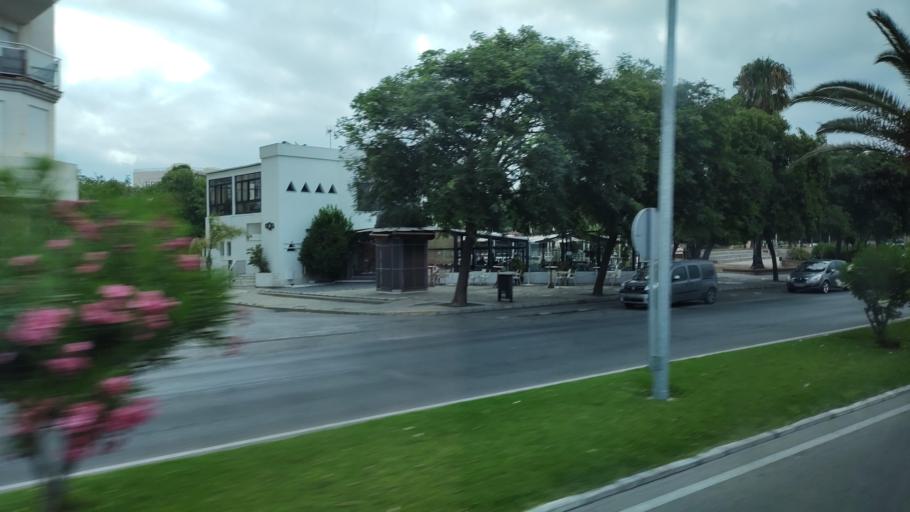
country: ES
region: Andalusia
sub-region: Provincia de Cadiz
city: La Linea de la Concepcion
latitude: 36.1606
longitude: -5.3553
